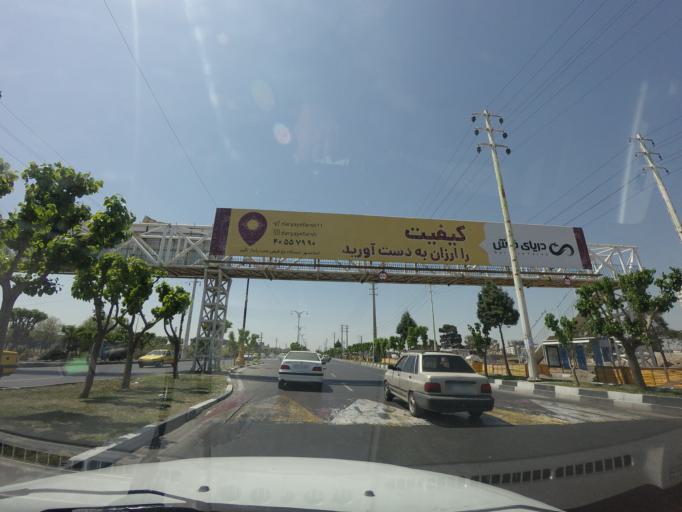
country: IR
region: Tehran
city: Eslamshahr
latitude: 35.5418
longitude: 51.2136
